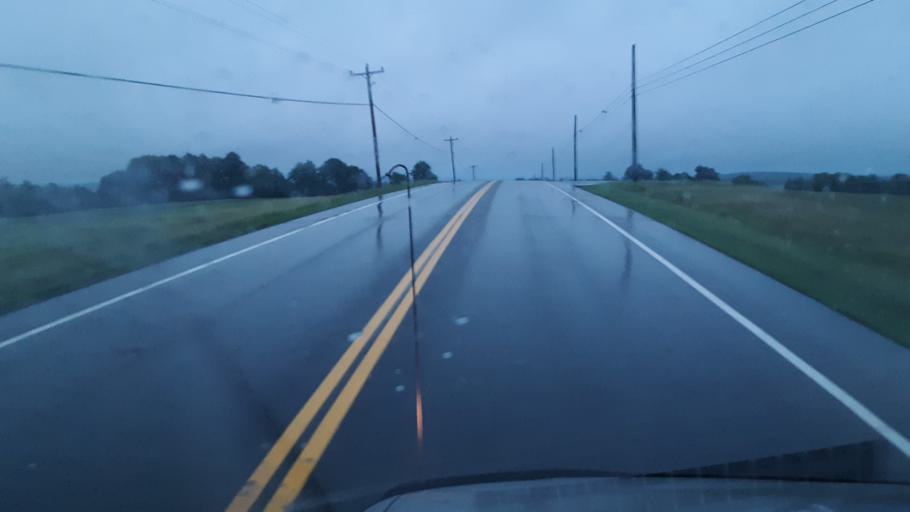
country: US
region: Maine
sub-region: Penobscot County
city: Patten
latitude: 45.9545
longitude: -68.4523
